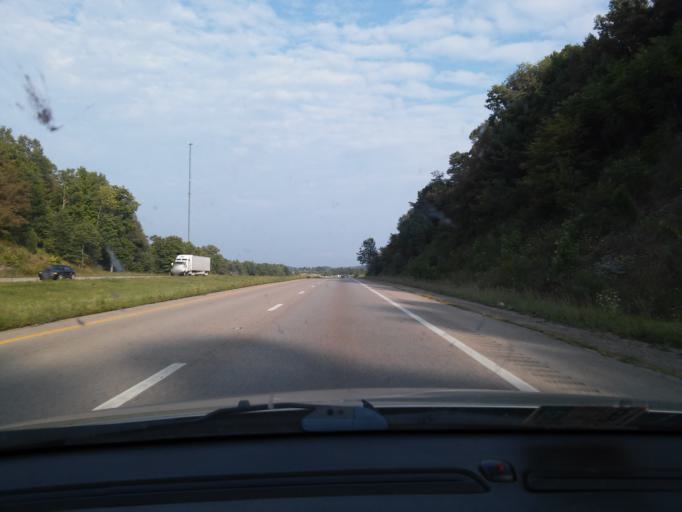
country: US
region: Ohio
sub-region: Gallia County
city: Gallipolis
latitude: 38.8876
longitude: -82.3493
